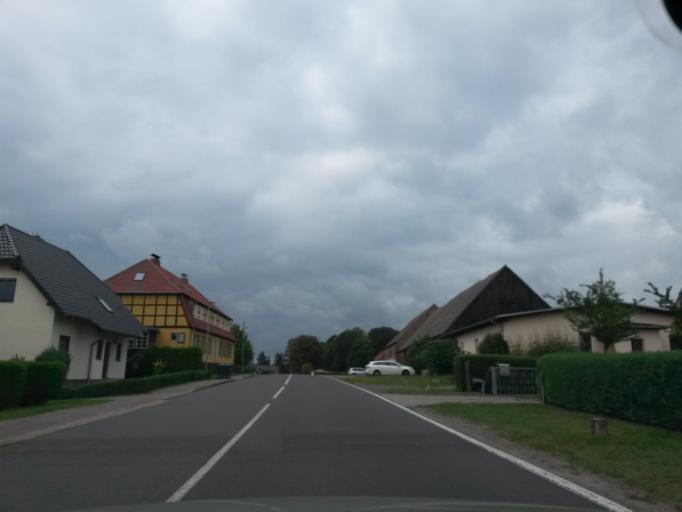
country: DE
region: Brandenburg
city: Angermunde
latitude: 53.1098
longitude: 13.9106
